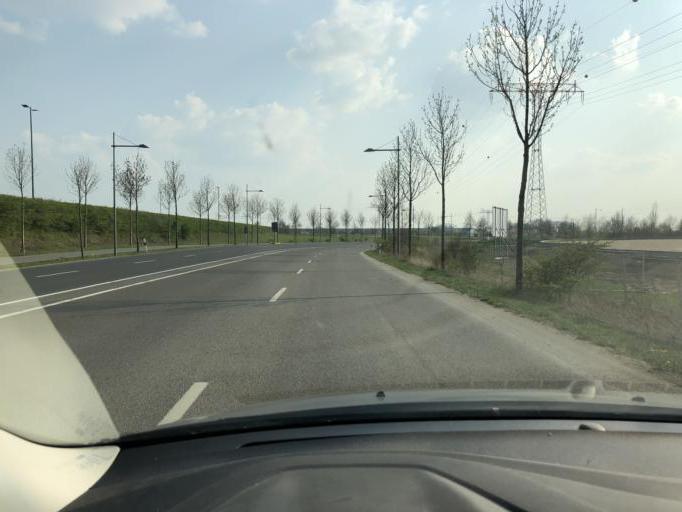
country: DE
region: Saxony
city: Taucha
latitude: 51.4026
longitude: 12.4321
